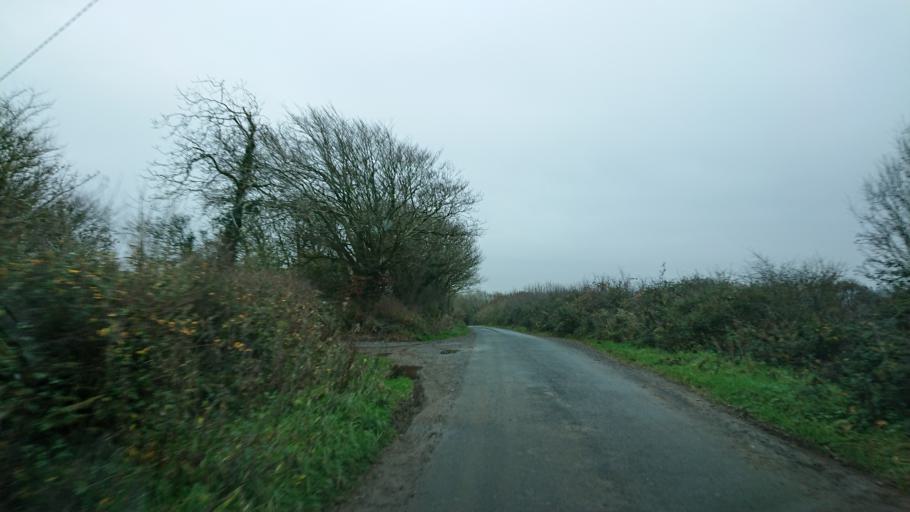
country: IE
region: Munster
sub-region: Waterford
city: Dunmore East
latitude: 52.1981
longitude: -7.0029
